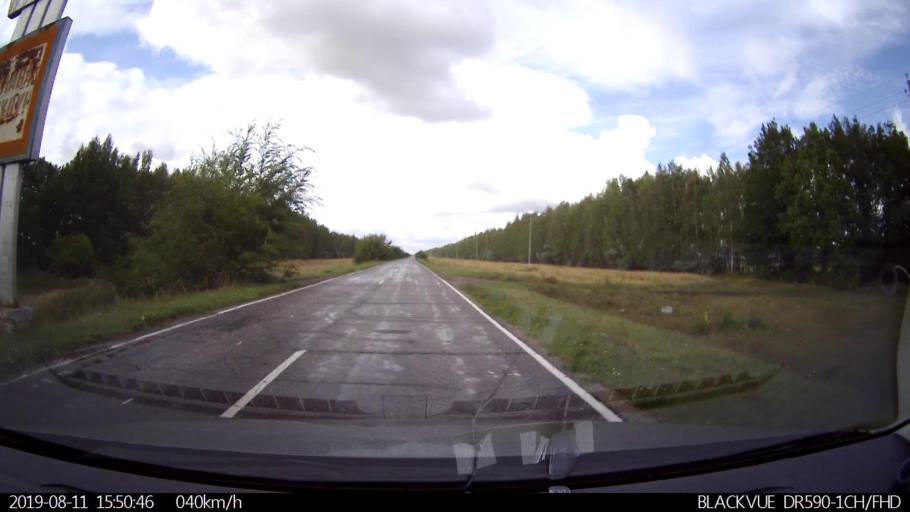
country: RU
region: Ulyanovsk
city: Ignatovka
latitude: 53.9140
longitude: 47.6559
